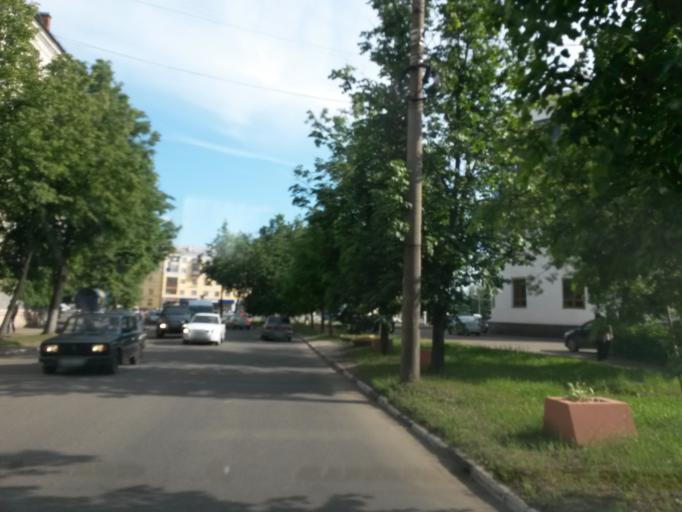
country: RU
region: Jaroslavl
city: Yaroslavl
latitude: 57.6350
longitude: 39.8598
